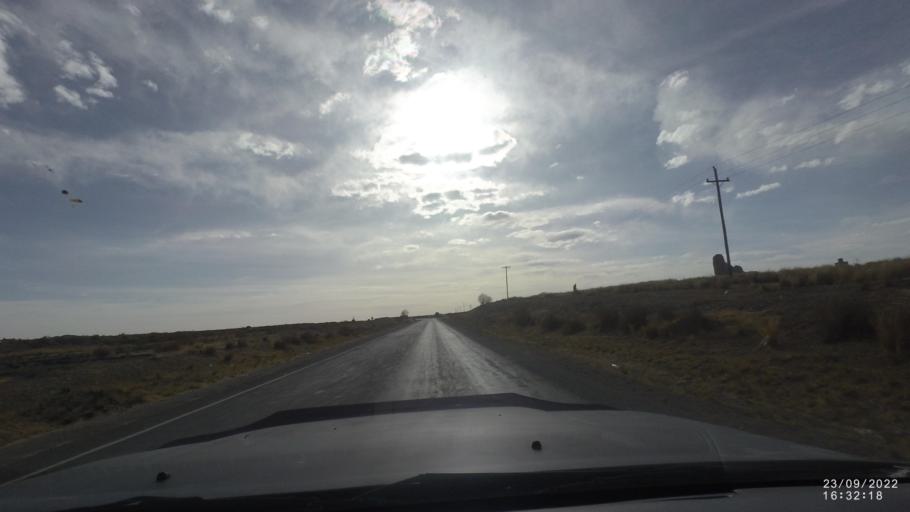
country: BO
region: Oruro
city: Machacamarca
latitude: -18.1638
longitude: -67.0039
